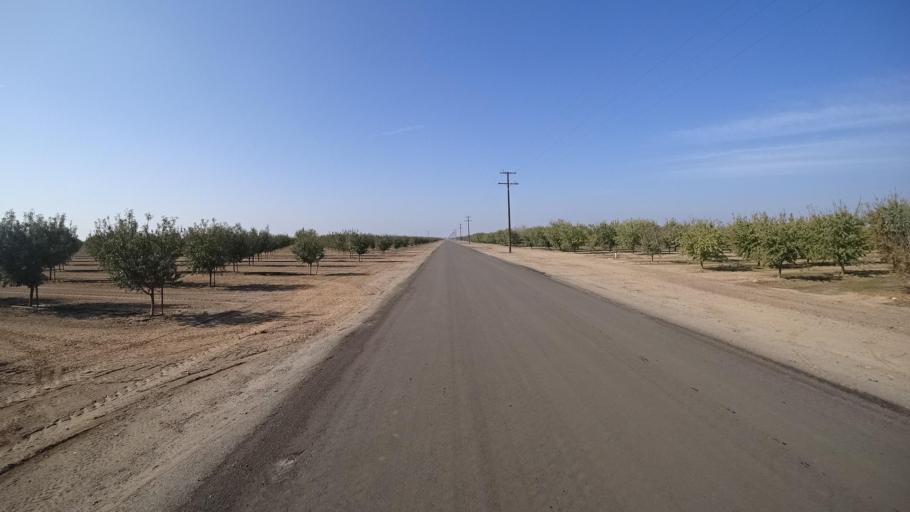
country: US
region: California
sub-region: Kern County
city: McFarland
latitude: 35.6601
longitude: -119.1743
